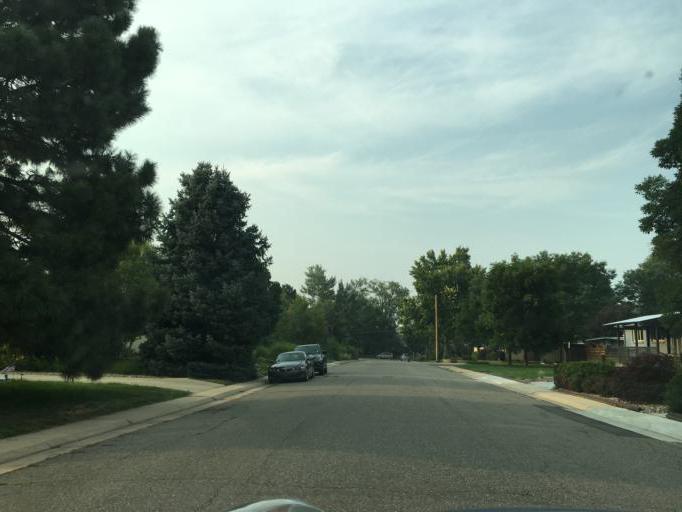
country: US
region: Colorado
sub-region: Arapahoe County
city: Glendale
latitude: 39.6896
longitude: -104.9340
